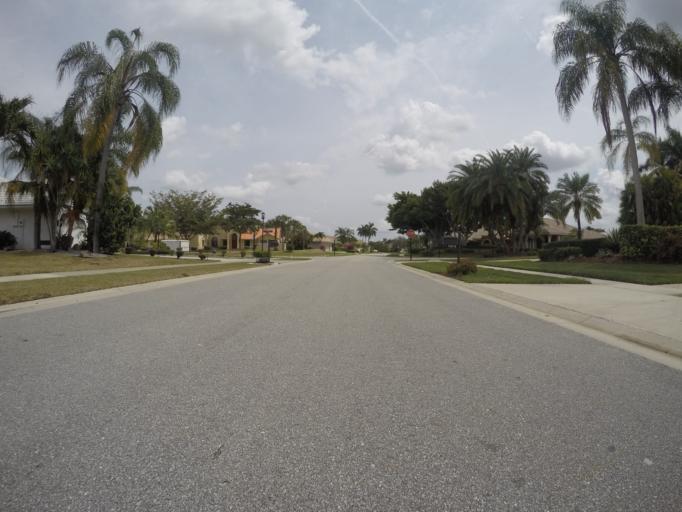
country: US
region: Florida
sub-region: Palm Beach County
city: Villages of Oriole
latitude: 26.4107
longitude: -80.2171
